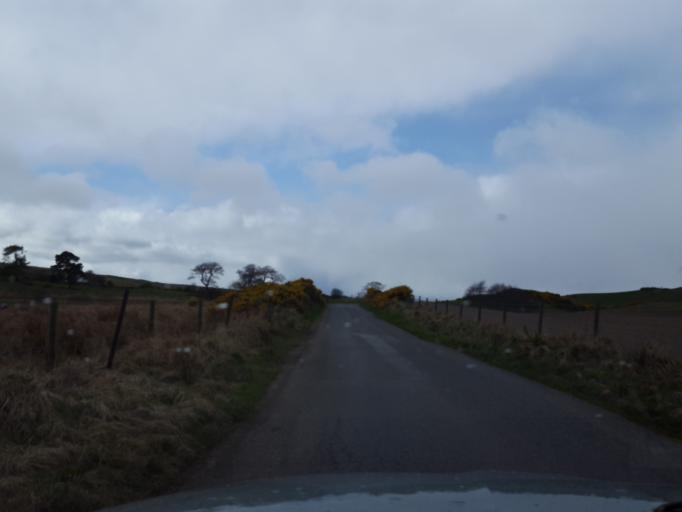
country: GB
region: Scotland
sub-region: Perth and Kinross
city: Scone
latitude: 56.4374
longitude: -3.3046
